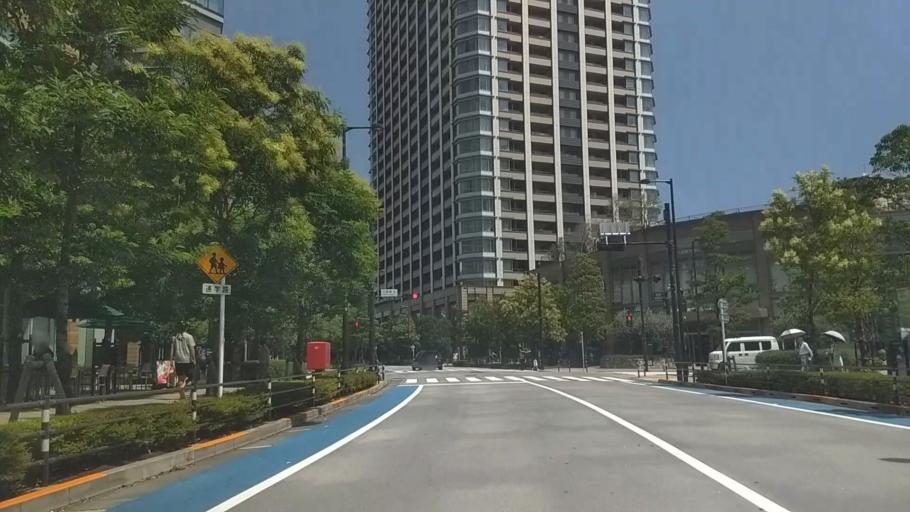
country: JP
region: Tokyo
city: Tokyo
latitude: 35.6212
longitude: 139.7311
